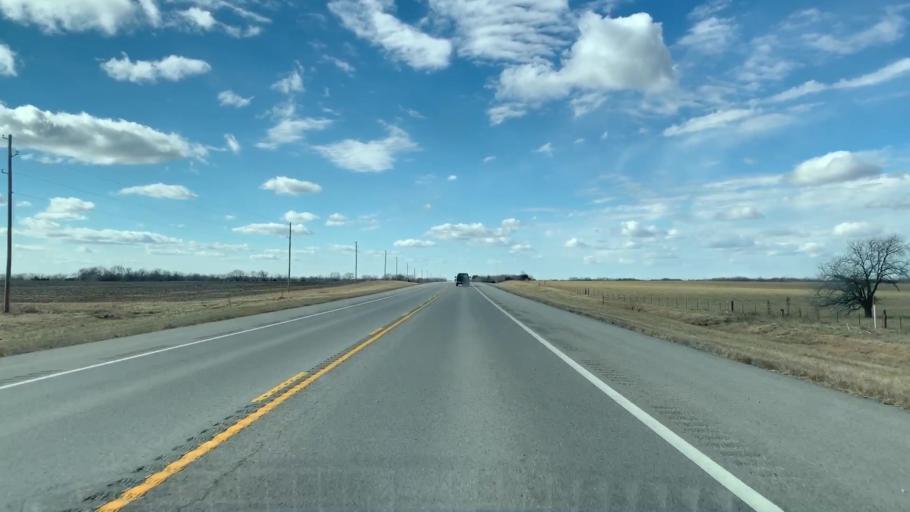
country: US
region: Kansas
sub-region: Labette County
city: Oswego
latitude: 37.3401
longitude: -95.0449
